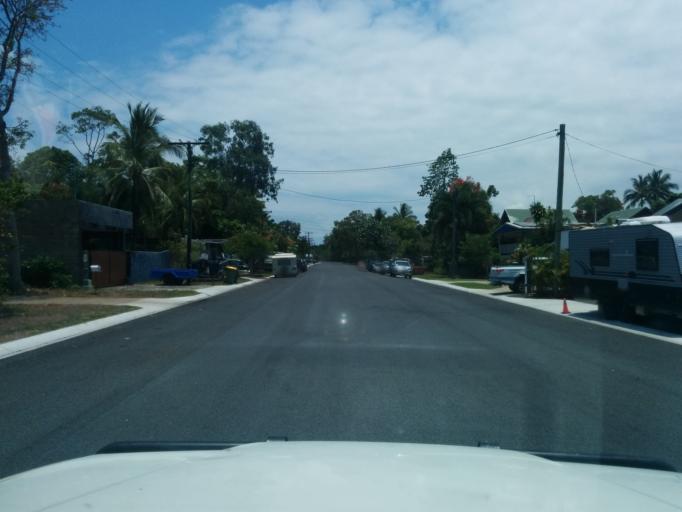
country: AU
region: Queensland
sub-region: Cairns
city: Yorkeys Knob
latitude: -16.8299
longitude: 145.7349
